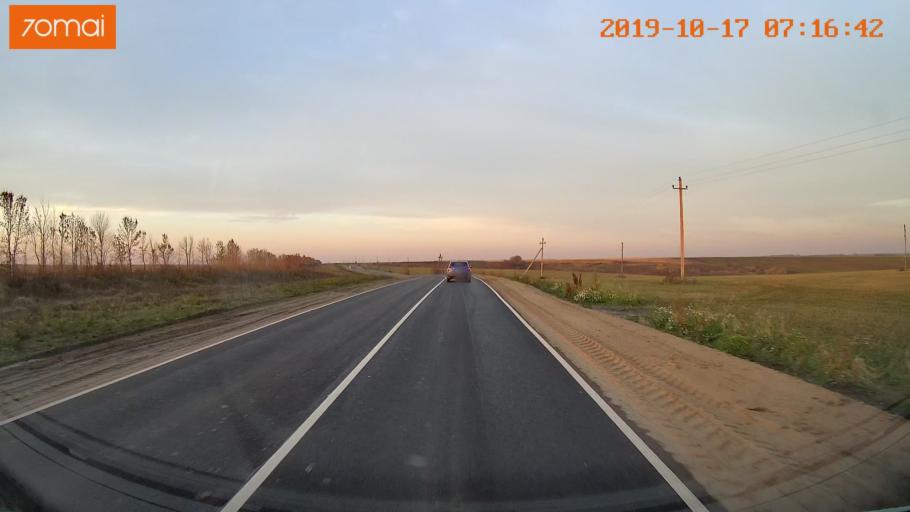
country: RU
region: Vladimir
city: Suzdal'
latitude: 56.3705
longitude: 40.2439
